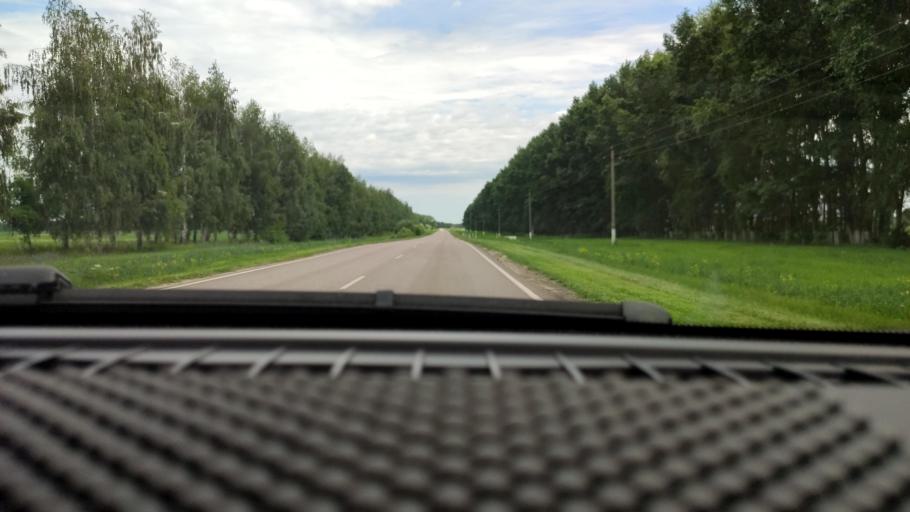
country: RU
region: Voronezj
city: Panino
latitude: 51.6599
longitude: 39.9891
